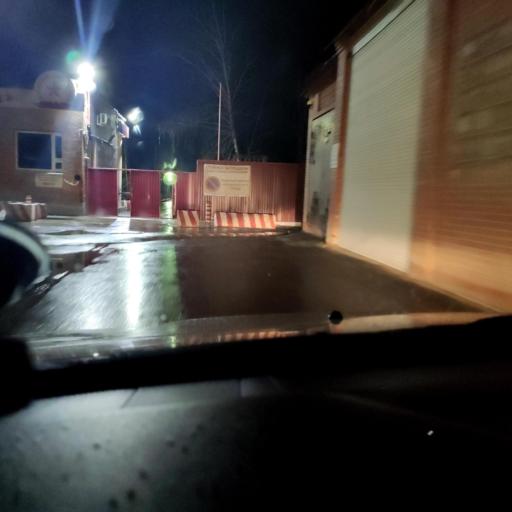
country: RU
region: Samara
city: Samara
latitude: 53.2566
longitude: 50.1847
